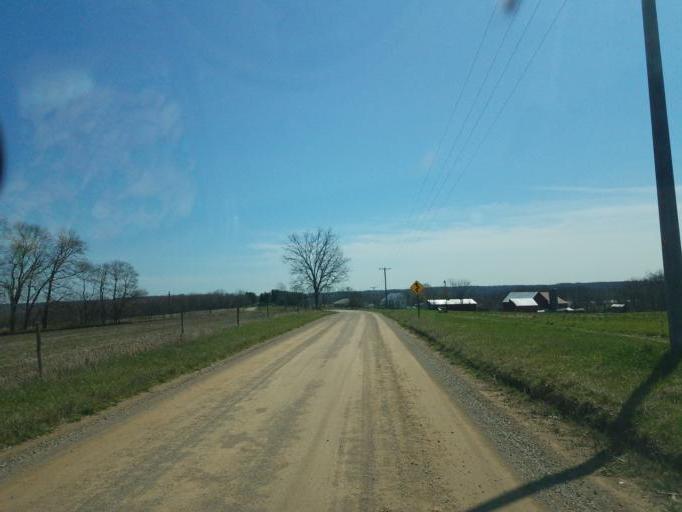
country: US
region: Ohio
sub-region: Knox County
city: Oak Hill
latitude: 40.3073
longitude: -82.2710
